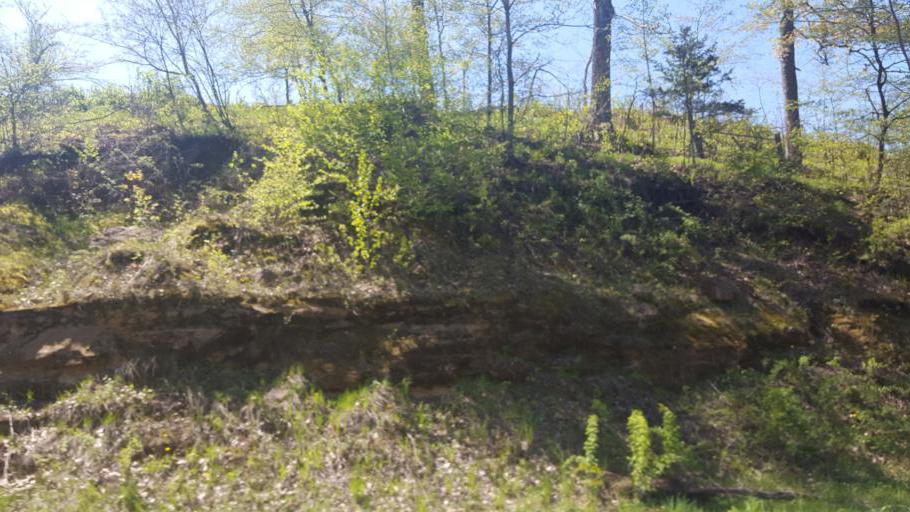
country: US
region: Wisconsin
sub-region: Vernon County
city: Hillsboro
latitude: 43.5770
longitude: -90.3704
